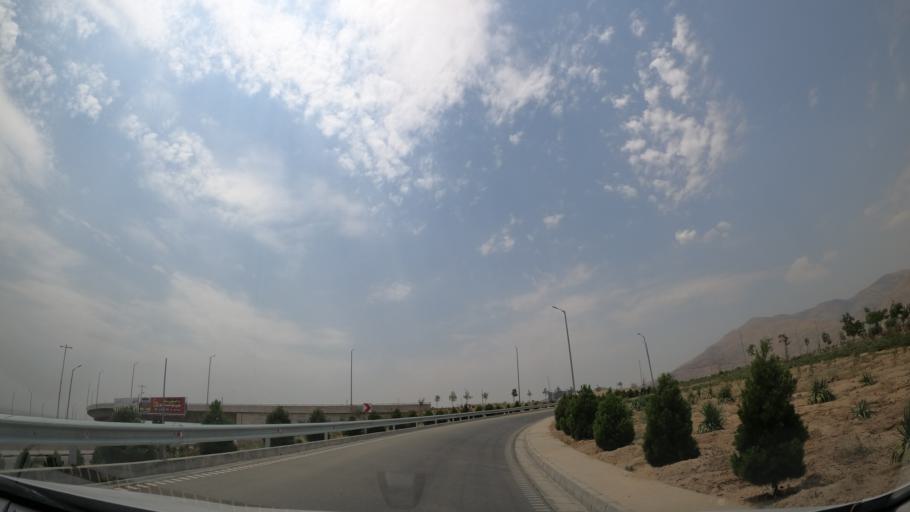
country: IR
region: Tehran
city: Shahr-e Qods
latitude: 35.7442
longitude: 51.1287
